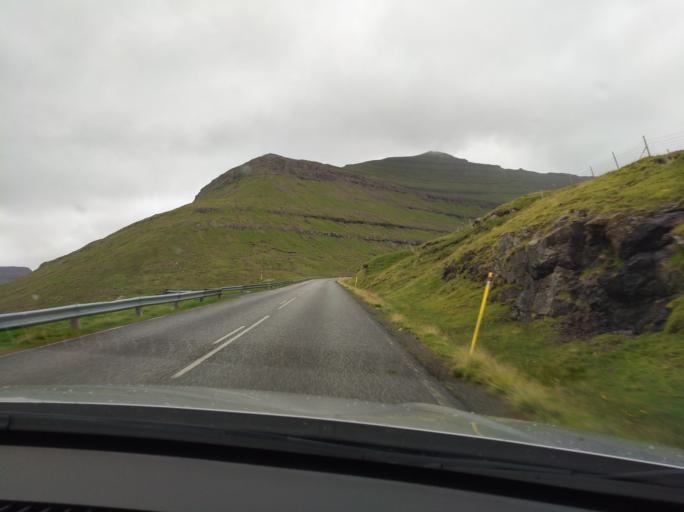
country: FO
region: Eysturoy
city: Fuglafjordur
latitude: 62.2224
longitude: -6.8764
